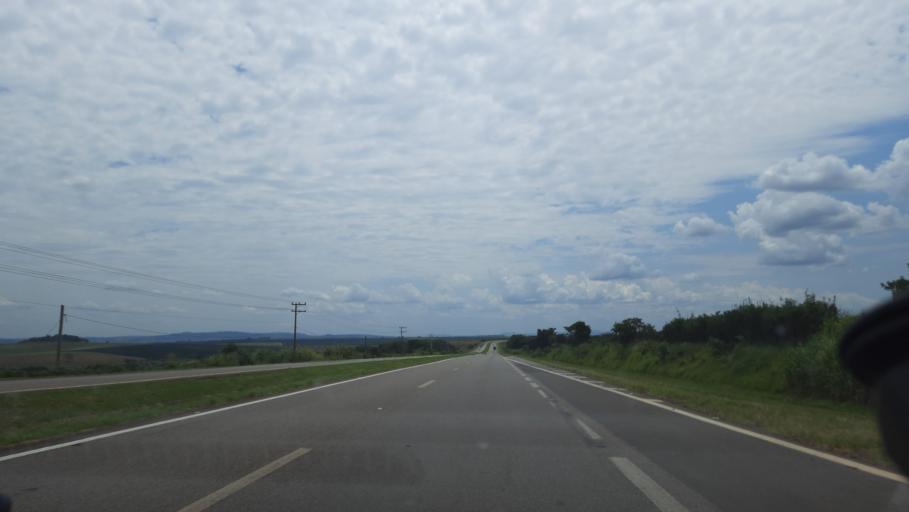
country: BR
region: Sao Paulo
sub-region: Casa Branca
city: Casa Branca
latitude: -21.7184
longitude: -47.0811
